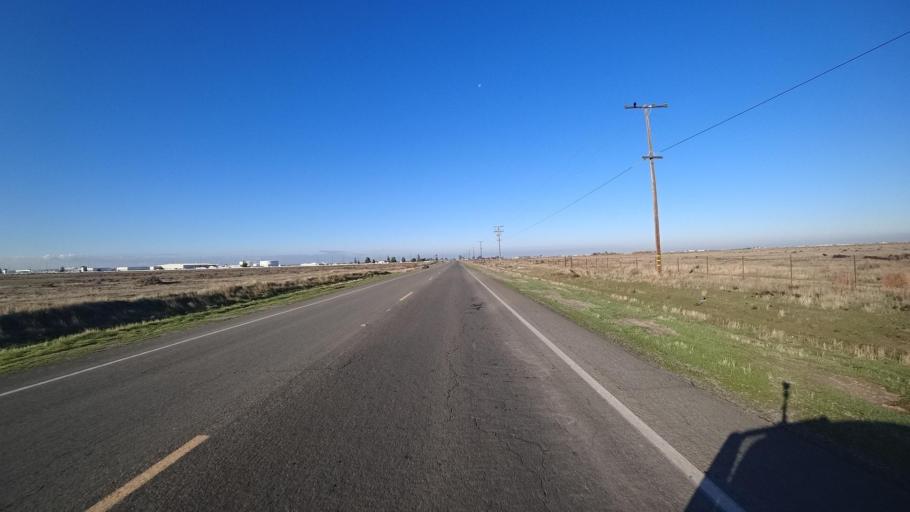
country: US
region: California
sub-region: Kern County
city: Delano
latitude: 35.7758
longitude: -119.3164
